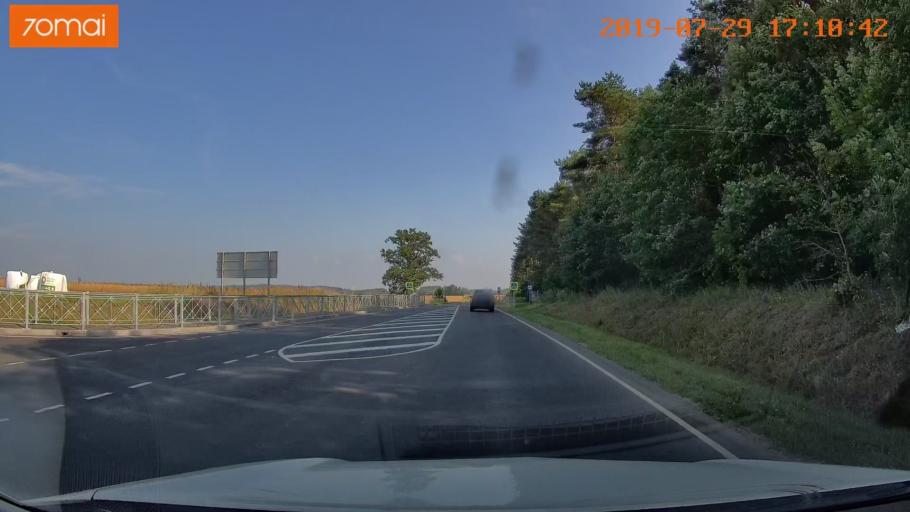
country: RU
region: Kaliningrad
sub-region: Gorod Kaliningrad
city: Kaliningrad
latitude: 54.8003
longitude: 20.3716
